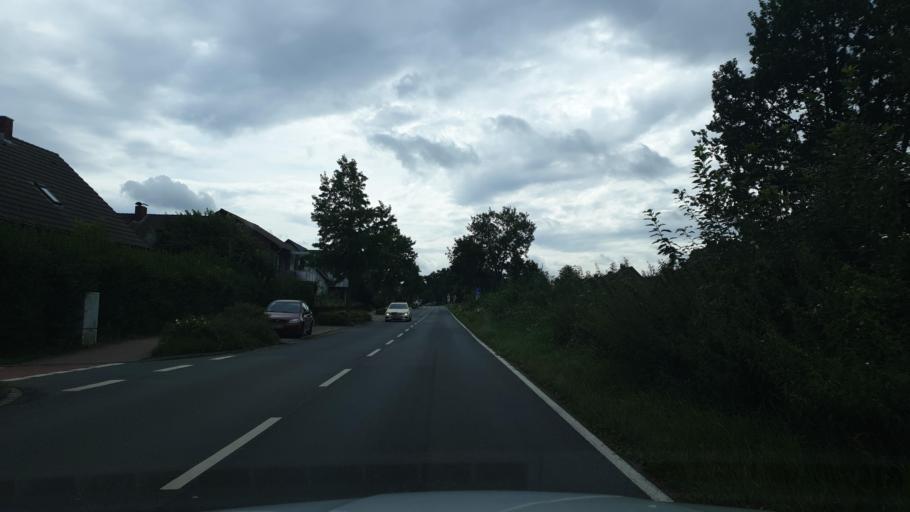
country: DE
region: Lower Saxony
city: Hasbergen
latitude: 52.2372
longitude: 7.9687
